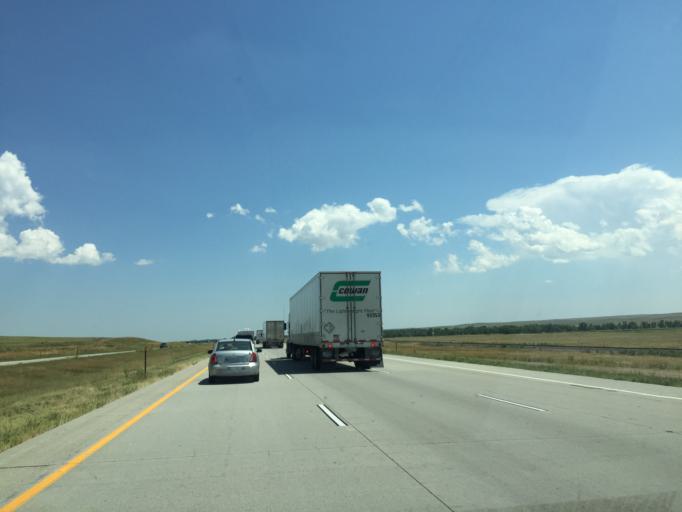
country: US
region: Colorado
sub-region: Lincoln County
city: Limon
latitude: 39.2898
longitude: -103.7930
